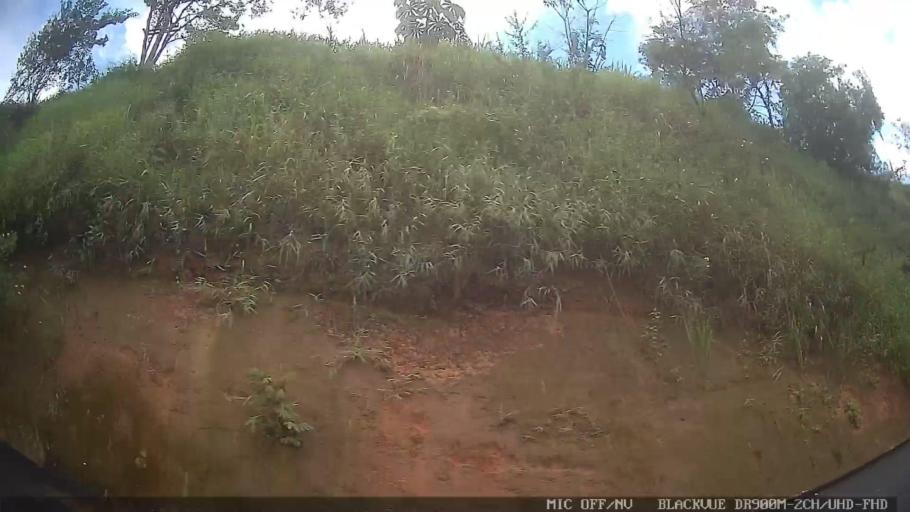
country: BR
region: Minas Gerais
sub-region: Extrema
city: Extrema
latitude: -22.8299
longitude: -46.2432
